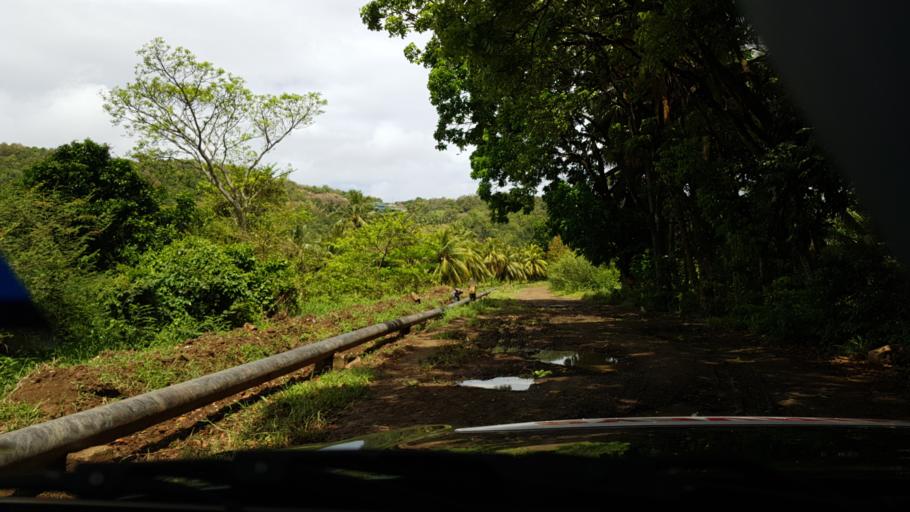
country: LC
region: Anse-la-Raye
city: Anse La Raye
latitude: 13.9535
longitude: -61.0289
